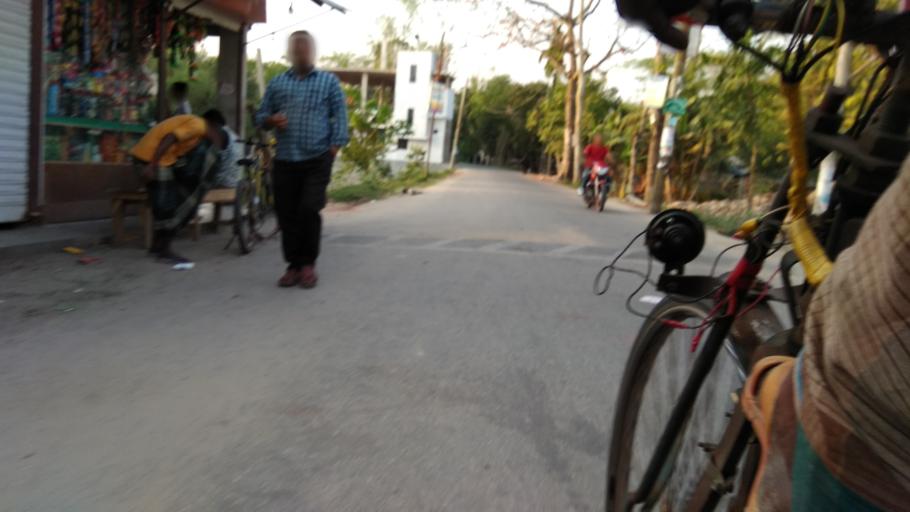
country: BD
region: Barisal
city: Mehendiganj
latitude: 22.9166
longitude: 90.4107
